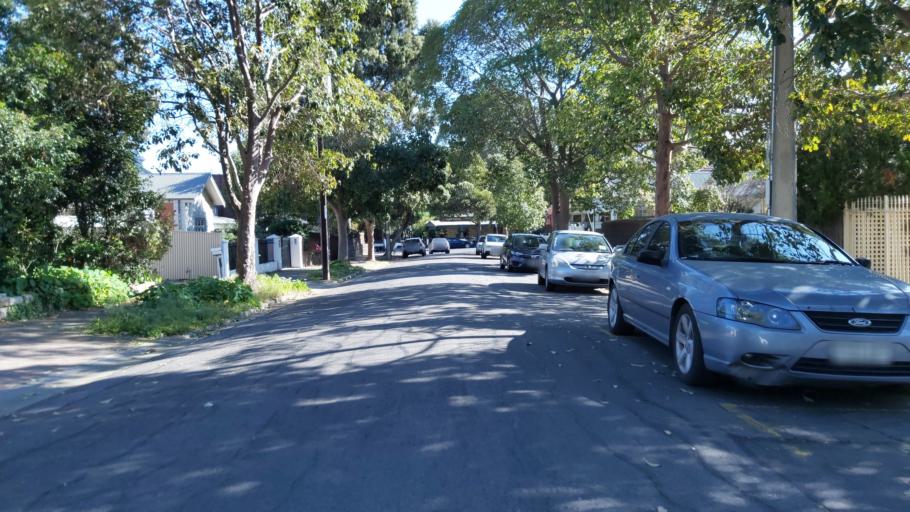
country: AU
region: South Australia
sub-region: Unley
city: Unley
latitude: -34.9456
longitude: 138.6016
